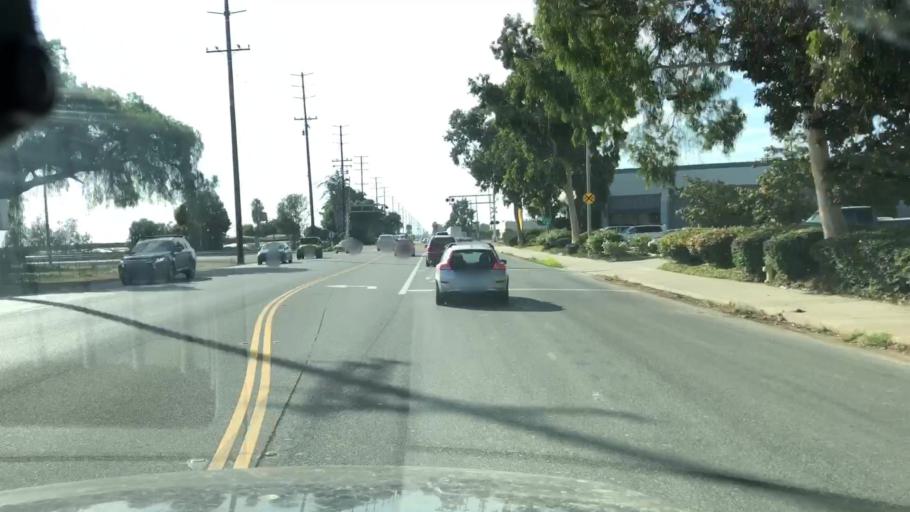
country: US
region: California
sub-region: Ventura County
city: Camarillo
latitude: 34.2055
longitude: -119.0398
